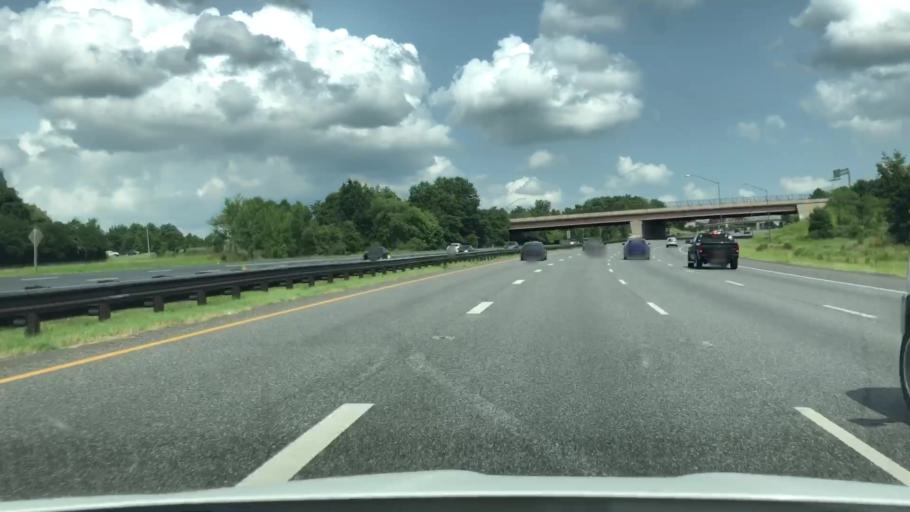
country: US
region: Maryland
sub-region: Prince George's County
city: Bowie
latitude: 38.9529
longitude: -76.7459
